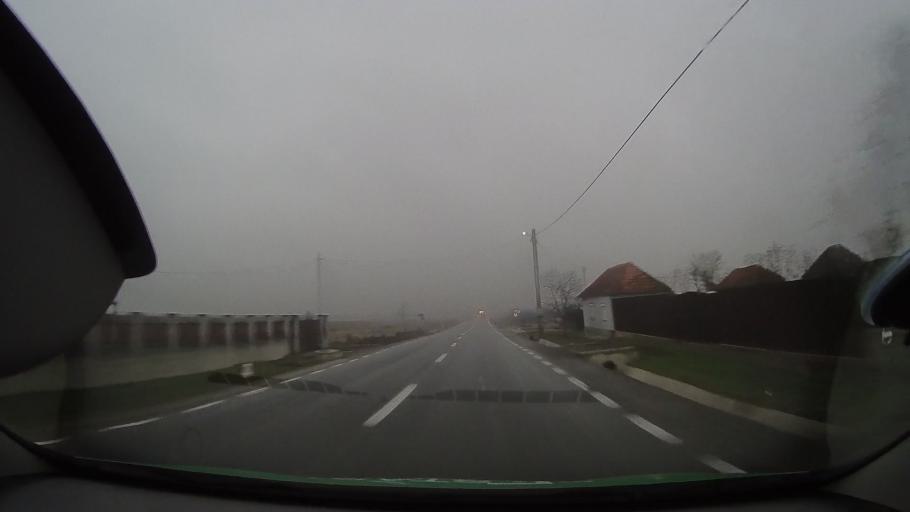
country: RO
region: Arad
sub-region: Comuna Craiova
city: Craiova
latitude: 46.6281
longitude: 21.9587
